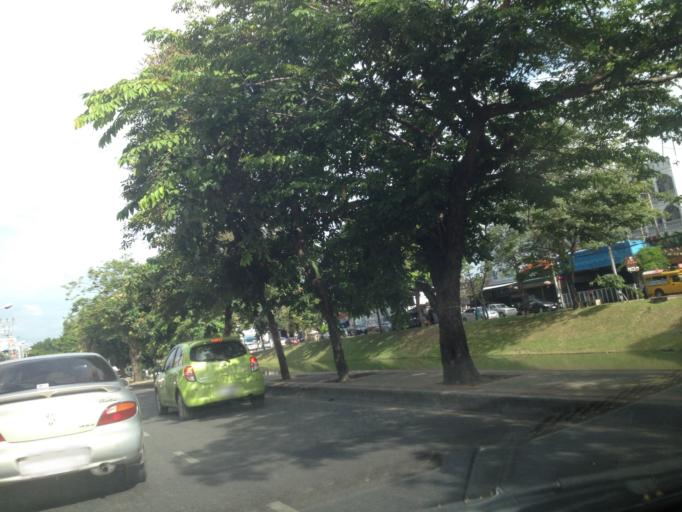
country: TH
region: Chiang Mai
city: Chiang Mai
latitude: 18.7956
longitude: 98.9908
